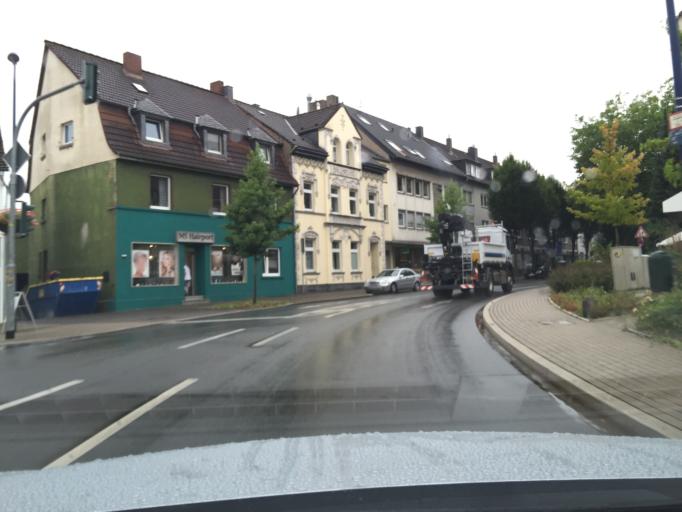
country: DE
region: North Rhine-Westphalia
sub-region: Regierungsbezirk Dusseldorf
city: Heiligenhaus
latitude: 51.3256
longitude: 6.9624
